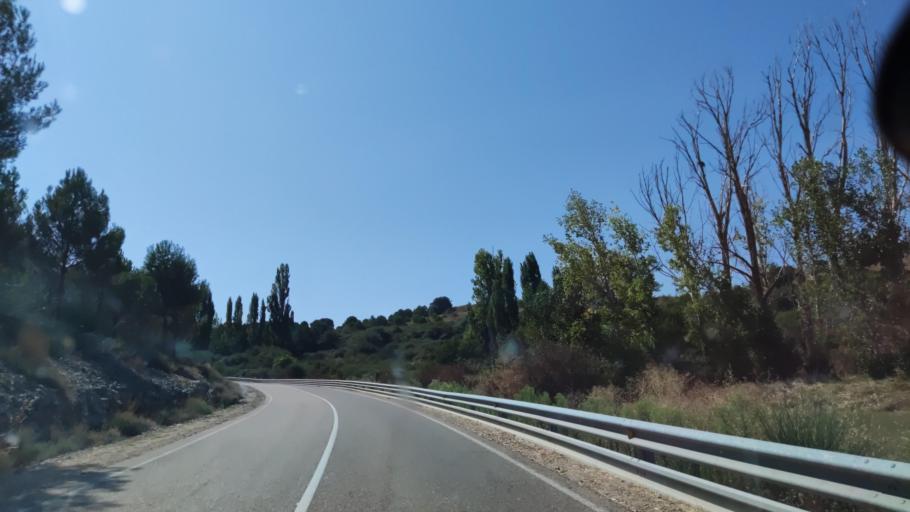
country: ES
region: Castille and Leon
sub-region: Provincia de Valladolid
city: Uruena
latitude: 41.7138
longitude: -5.1972
